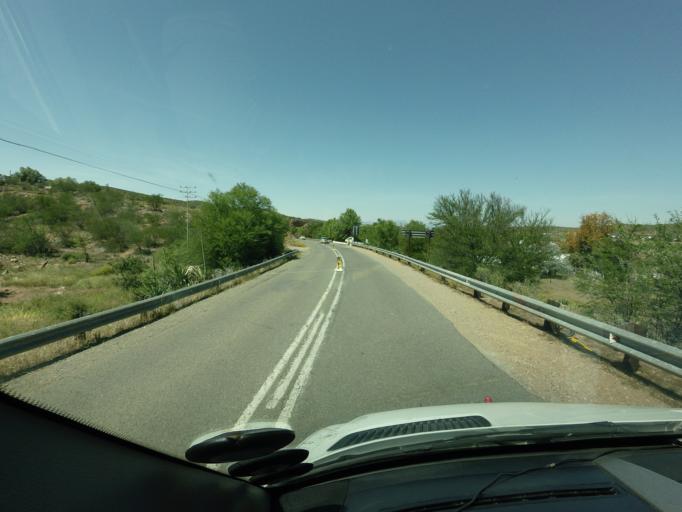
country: ZA
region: Western Cape
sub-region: Eden District Municipality
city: Oudtshoorn
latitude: -33.4856
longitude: 22.2474
